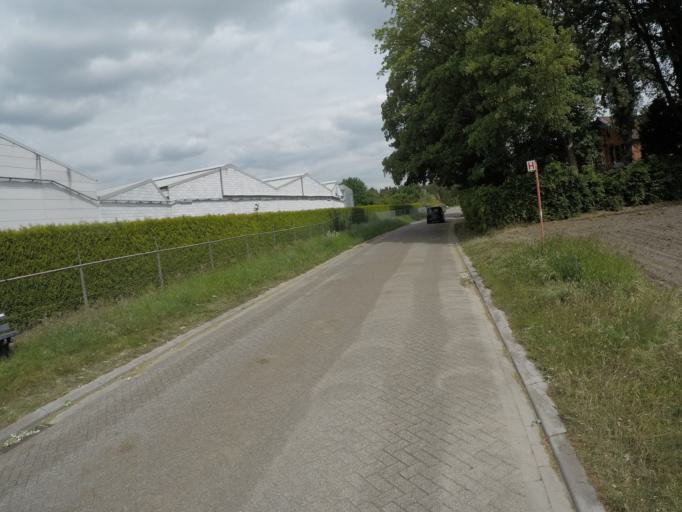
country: BE
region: Flanders
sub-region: Provincie Antwerpen
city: Zoersel
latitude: 51.2967
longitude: 4.6789
